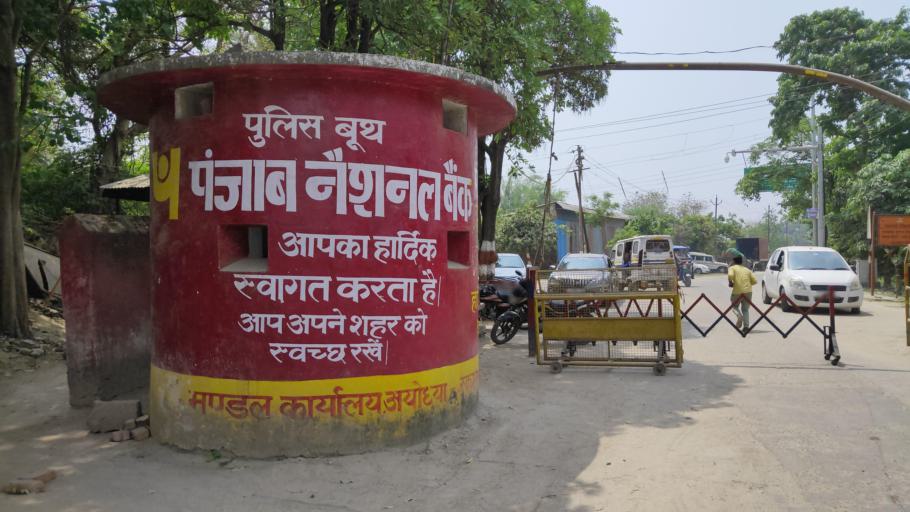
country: IN
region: Uttar Pradesh
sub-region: Faizabad
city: Ayodhya
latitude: 26.7856
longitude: 82.1788
